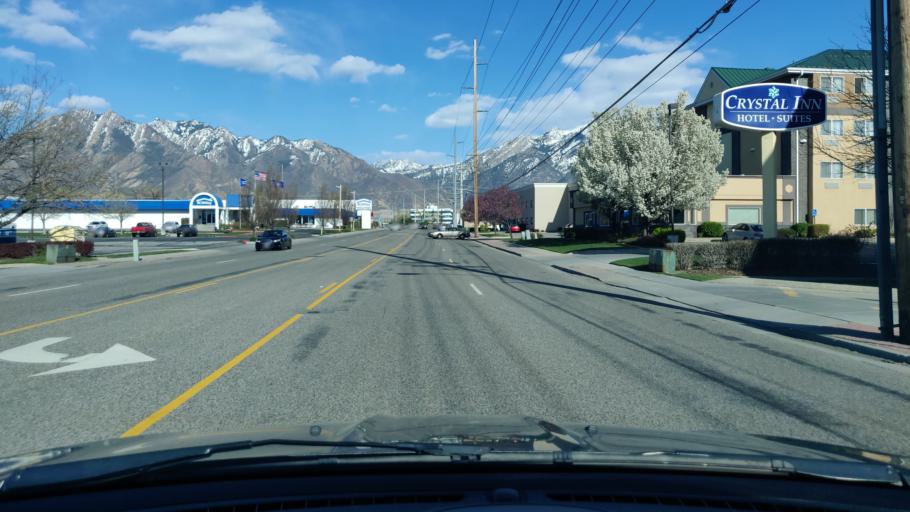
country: US
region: Utah
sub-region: Salt Lake County
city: Midvale
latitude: 40.6317
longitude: -111.8692
